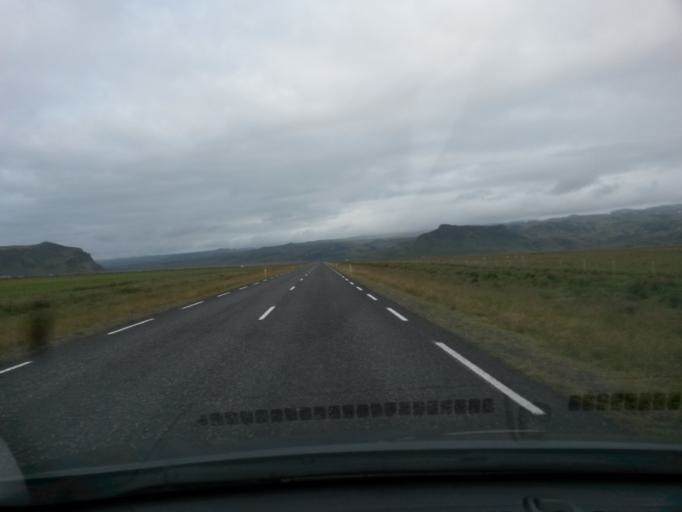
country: IS
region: South
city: Vestmannaeyjar
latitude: 63.4437
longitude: -19.2001
